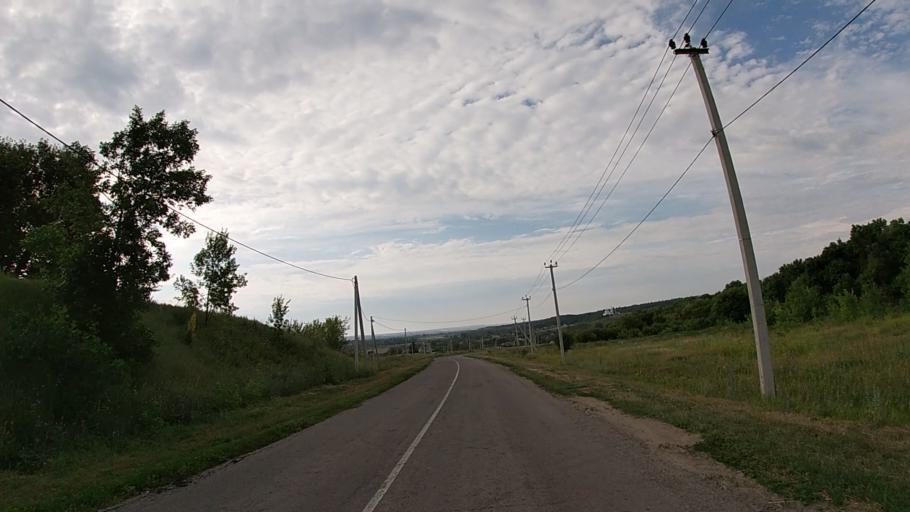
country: RU
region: Belgorod
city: Severnyy
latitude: 50.7177
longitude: 36.5891
